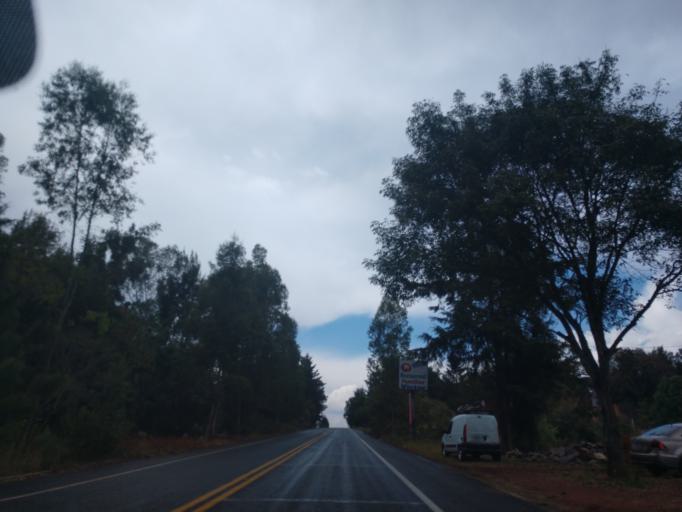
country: MX
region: Jalisco
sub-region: Mazamitla
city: Mazamitla
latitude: 19.9452
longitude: -103.0665
